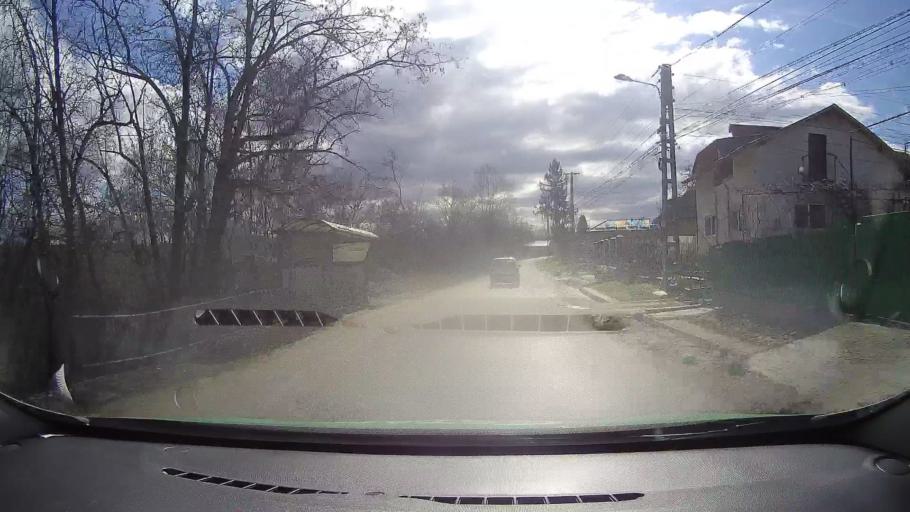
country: RO
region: Dambovita
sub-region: Oras Pucioasa
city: Pucioasa
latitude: 45.0648
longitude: 25.4246
